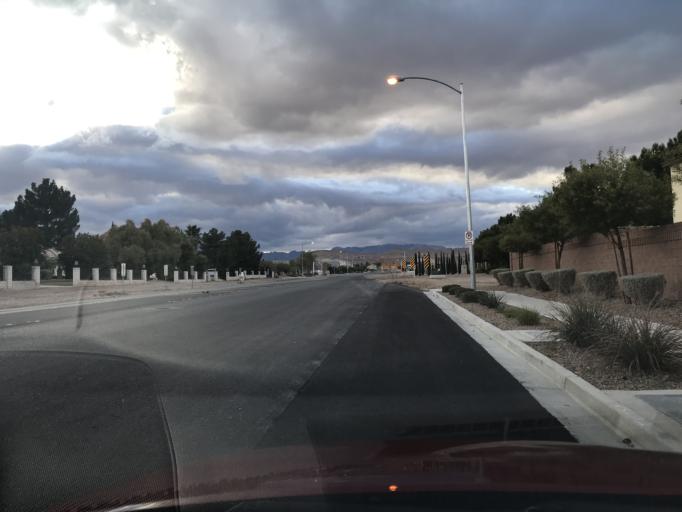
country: US
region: Nevada
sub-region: Clark County
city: Enterprise
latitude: 36.0400
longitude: -115.2732
